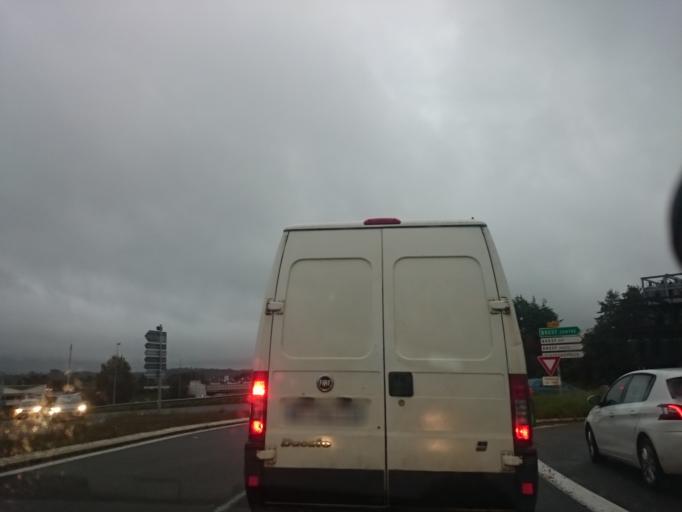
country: FR
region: Brittany
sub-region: Departement du Finistere
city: Le Relecq-Kerhuon
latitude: 48.3994
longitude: -4.4105
